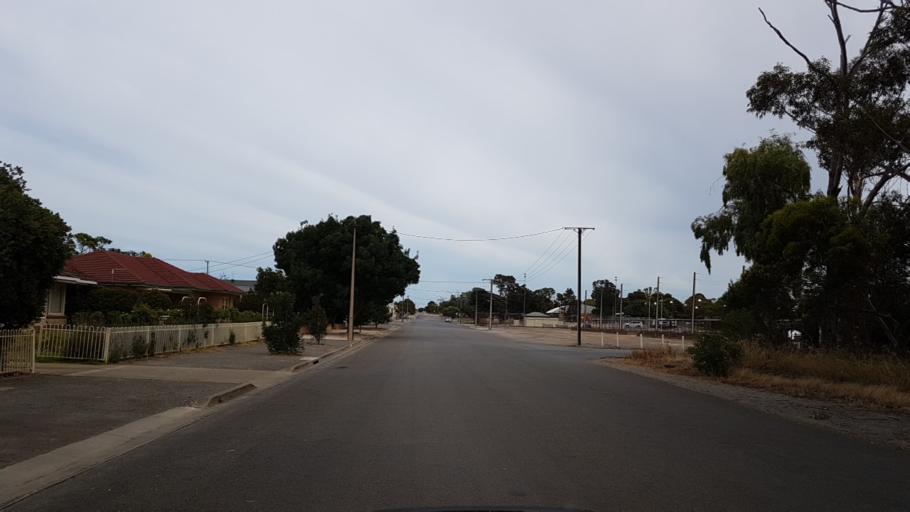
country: AU
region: South Australia
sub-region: Yorke Peninsula
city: Port Victoria
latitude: -34.7690
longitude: 137.6000
